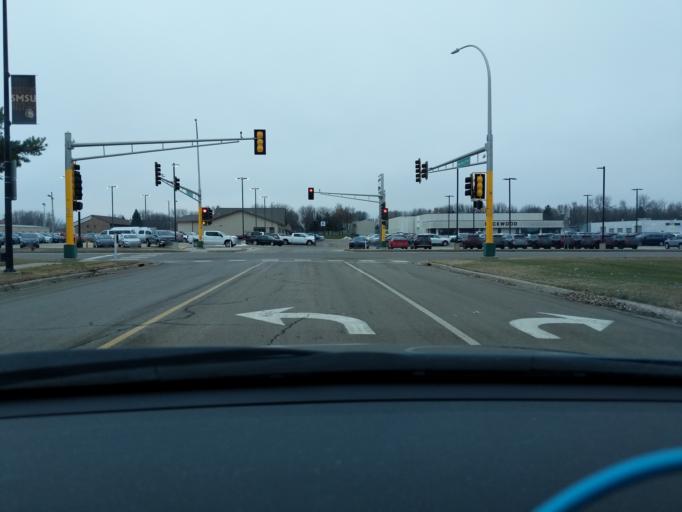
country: US
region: Minnesota
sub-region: Lyon County
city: Marshall
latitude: 44.4508
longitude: -95.7661
